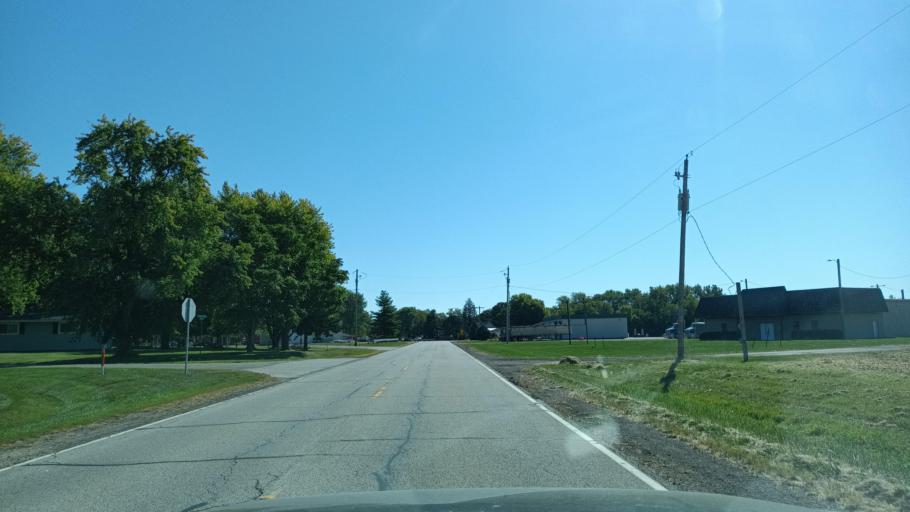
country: US
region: Illinois
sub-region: Peoria County
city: Elmwood
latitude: 40.8404
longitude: -89.8929
